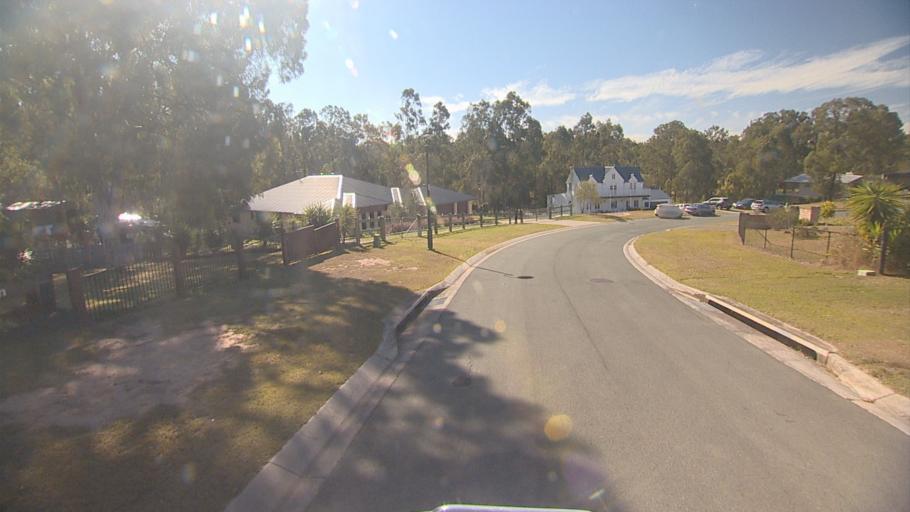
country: AU
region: Queensland
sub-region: Ipswich
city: Springfield Lakes
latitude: -27.7293
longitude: 152.9353
